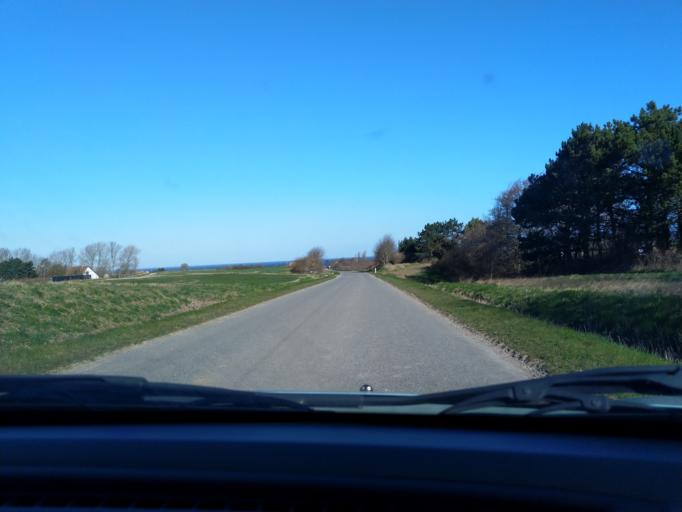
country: DK
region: Zealand
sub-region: Kalundborg Kommune
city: Kalundborg
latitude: 55.7434
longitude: 10.9526
